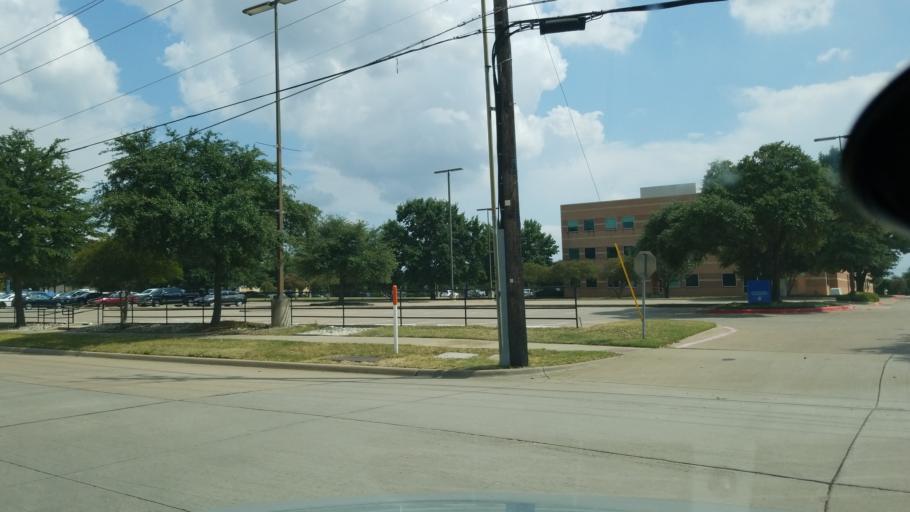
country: US
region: Texas
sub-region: Dallas County
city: Garland
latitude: 32.9187
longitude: -96.6634
